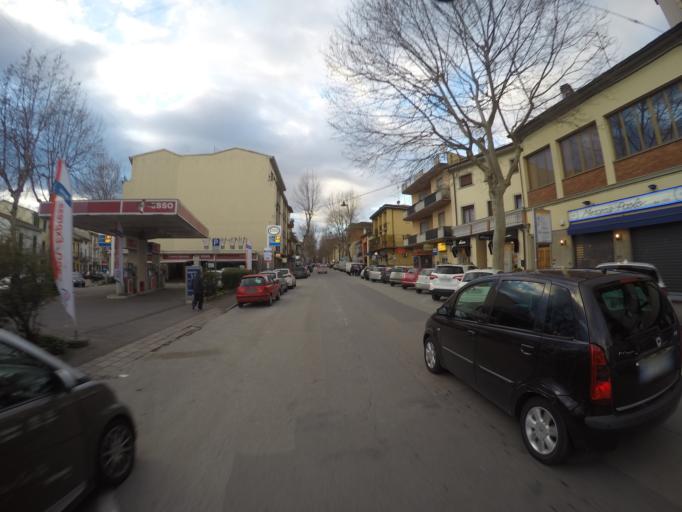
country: IT
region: Tuscany
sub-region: Provincia di Prato
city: Prato
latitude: 43.8703
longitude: 11.1110
